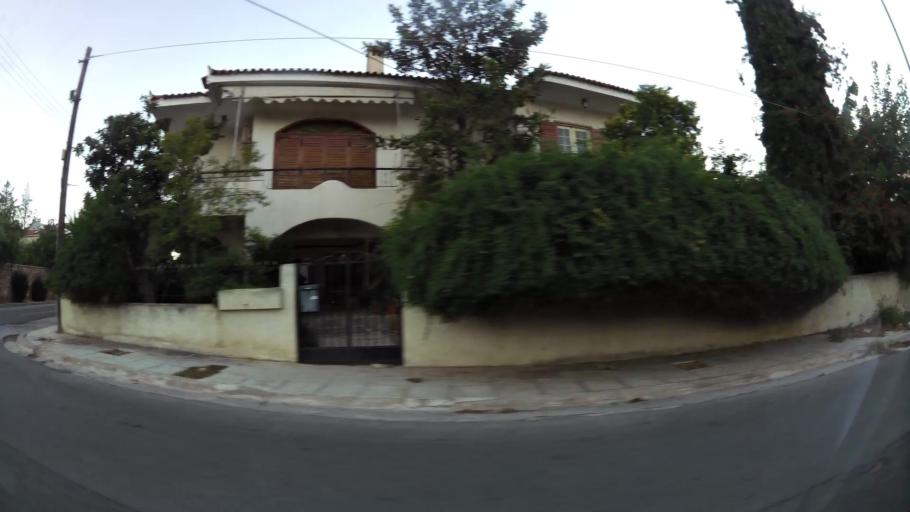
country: GR
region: Attica
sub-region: Nomarchia Anatolikis Attikis
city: Paiania
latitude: 37.9572
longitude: 23.8507
